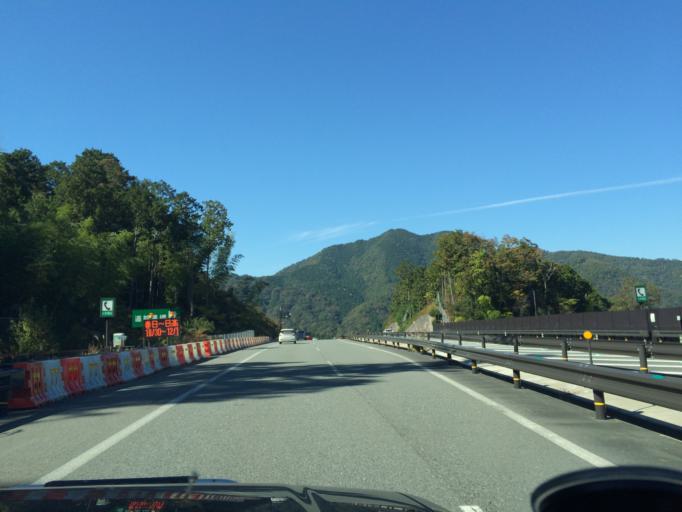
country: JP
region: Hyogo
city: Toyooka
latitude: 35.3385
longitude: 134.8163
